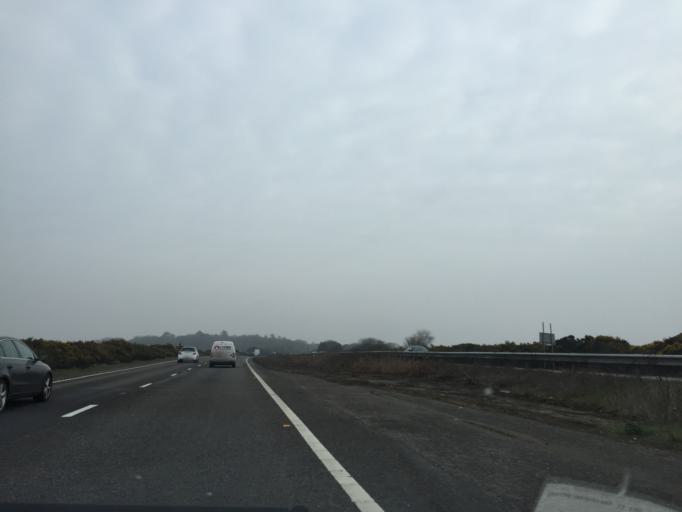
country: GB
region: England
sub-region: Hampshire
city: Bransgore
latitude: 50.8750
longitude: -1.6916
